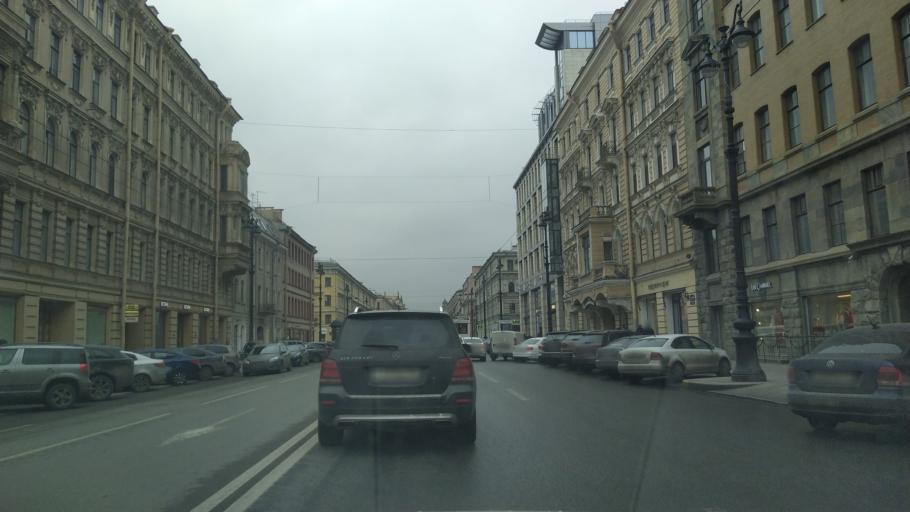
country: RU
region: St.-Petersburg
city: Centralniy
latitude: 59.9274
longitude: 30.3747
